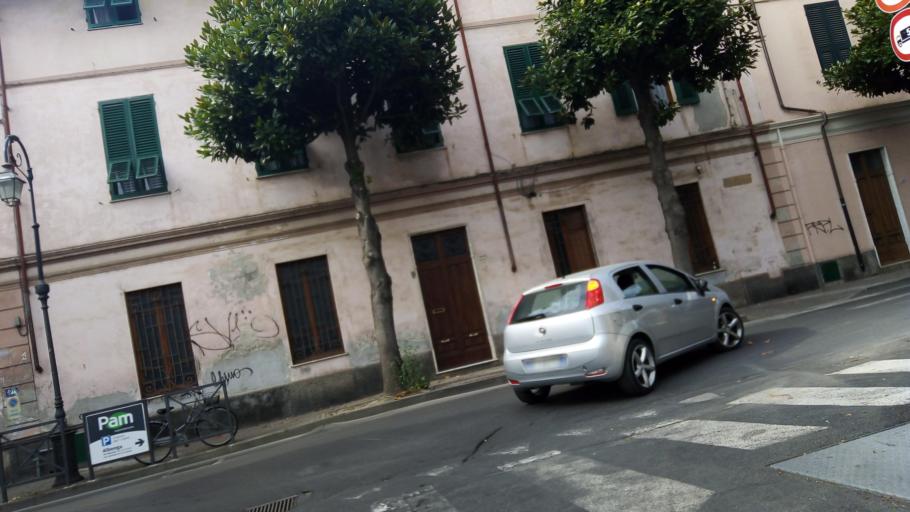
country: IT
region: Liguria
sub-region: Provincia di Savona
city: Albenga
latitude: 44.0480
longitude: 8.2201
